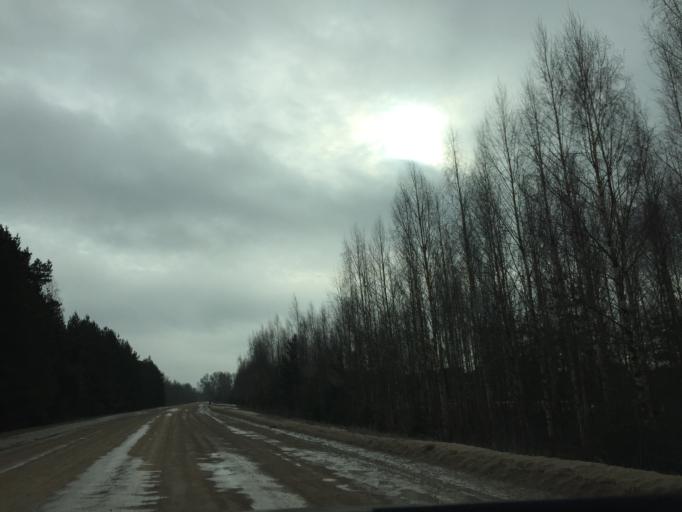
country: LV
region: Rundales
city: Pilsrundale
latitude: 56.5426
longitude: 23.9927
